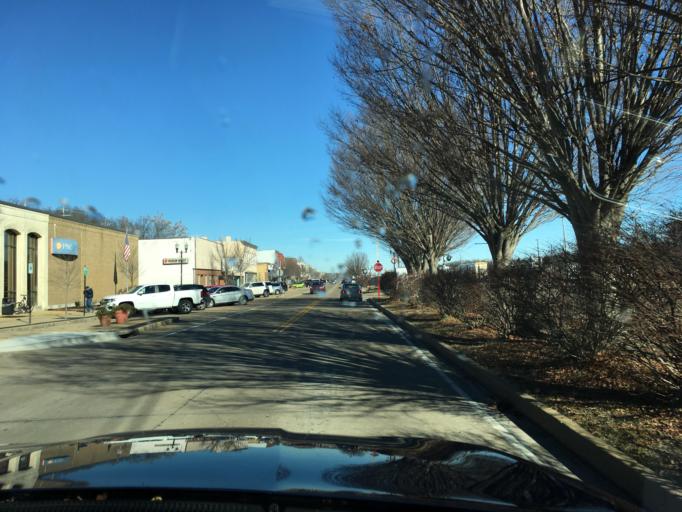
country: US
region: Missouri
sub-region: Jefferson County
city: De Soto
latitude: 38.1370
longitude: -90.5545
